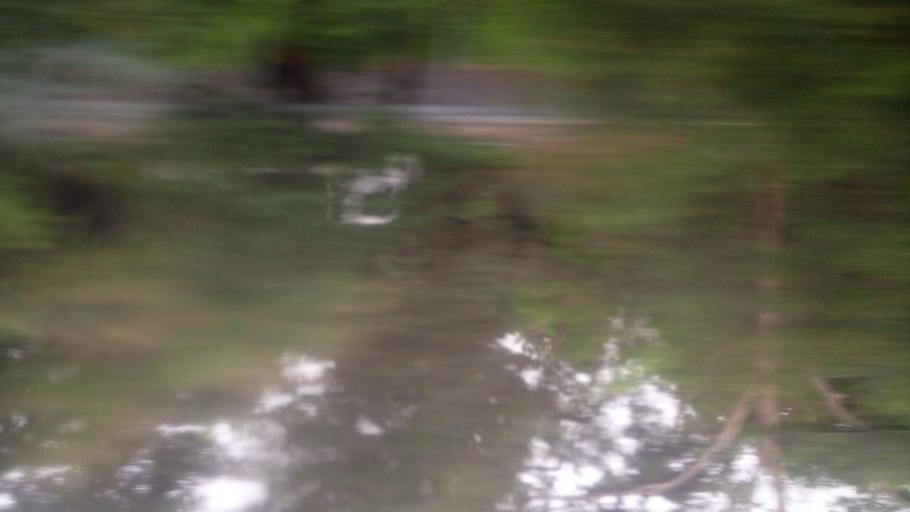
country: AU
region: New South Wales
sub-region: Blue Mountains Municipality
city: Blaxland
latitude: -33.7012
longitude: 150.5730
